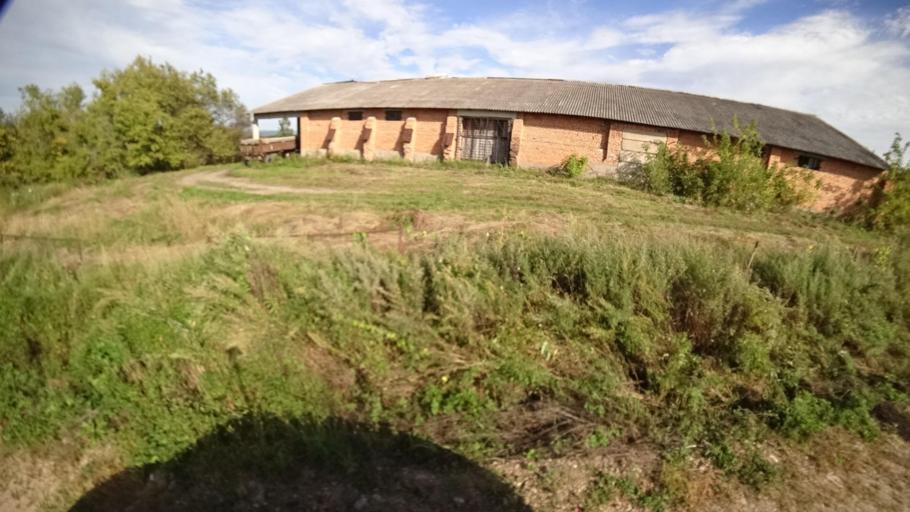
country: RU
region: Primorskiy
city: Dostoyevka
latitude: 44.3029
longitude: 133.4554
